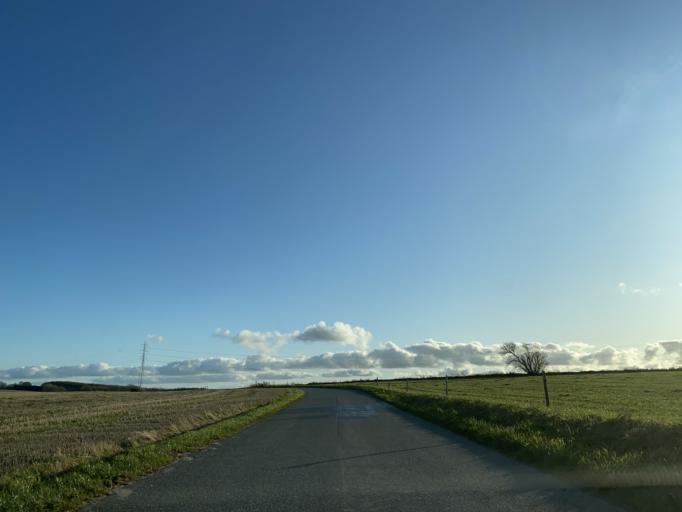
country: DK
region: Central Jutland
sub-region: Viborg Kommune
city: Bjerringbro
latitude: 56.3520
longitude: 9.7172
